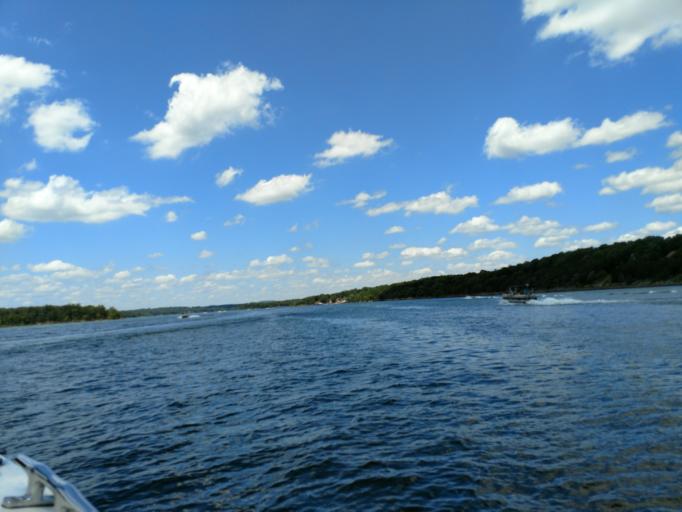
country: US
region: Missouri
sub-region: Barry County
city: Shell Knob
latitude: 36.5900
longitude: -93.5423
